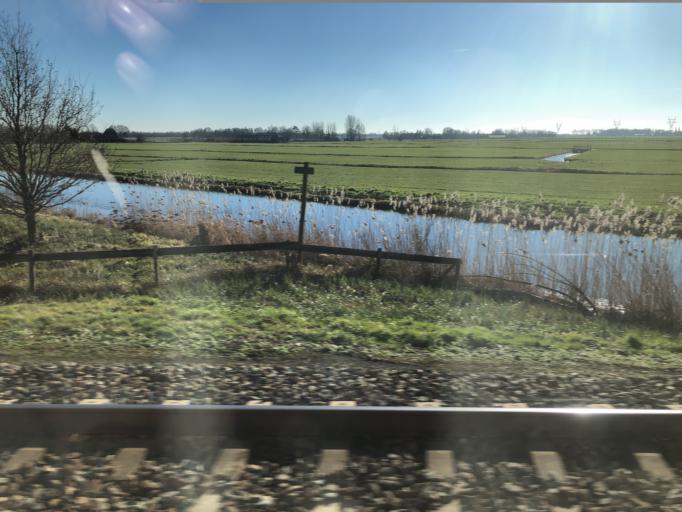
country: NL
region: North Holland
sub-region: Gemeente Weesp
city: Weesp
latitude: 52.3157
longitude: 5.0885
